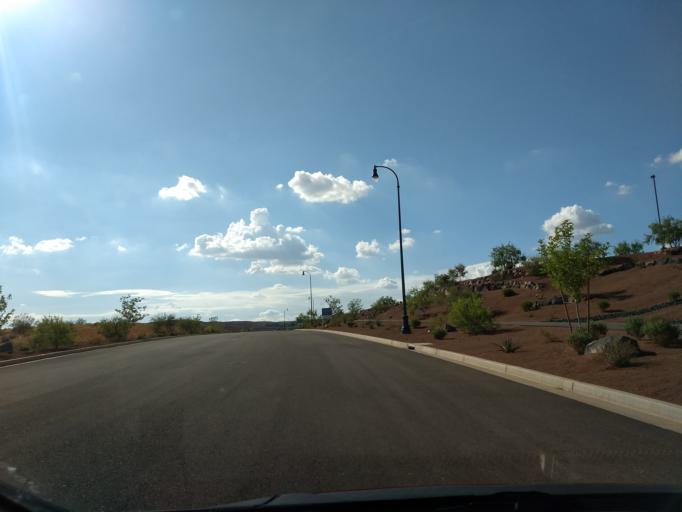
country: US
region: Utah
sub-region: Washington County
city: Washington
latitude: 37.1417
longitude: -113.5130
